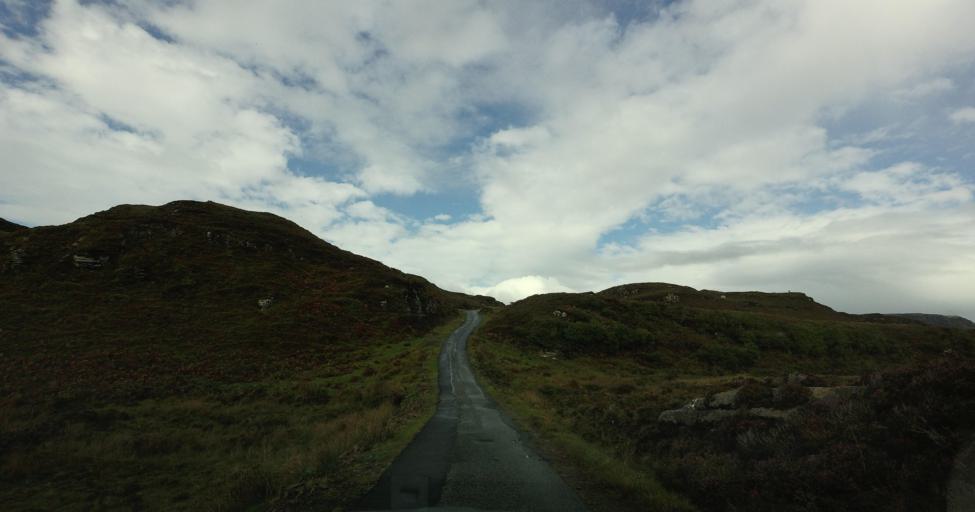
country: GB
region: Scotland
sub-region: Highland
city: Isle of Skye
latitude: 57.1432
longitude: -6.0897
